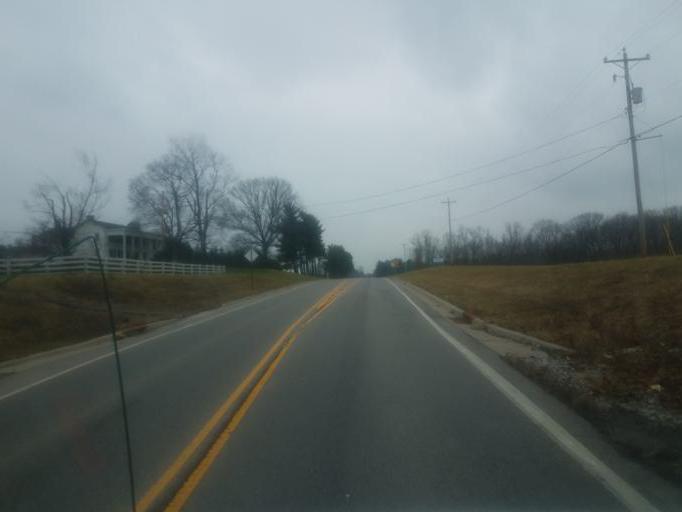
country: US
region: Ohio
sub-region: Franklin County
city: Westerville
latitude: 40.1743
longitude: -82.9537
